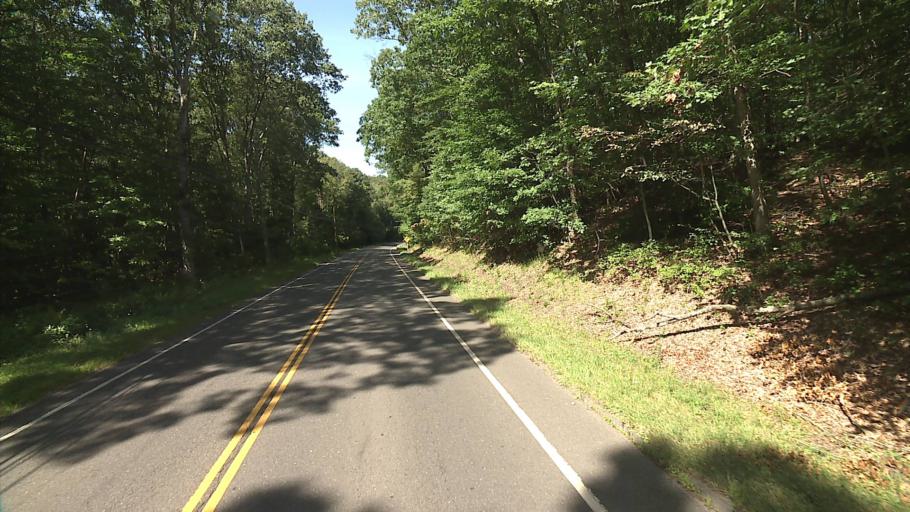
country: US
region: Connecticut
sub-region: New Haven County
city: Middlebury
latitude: 41.4854
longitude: -73.1597
